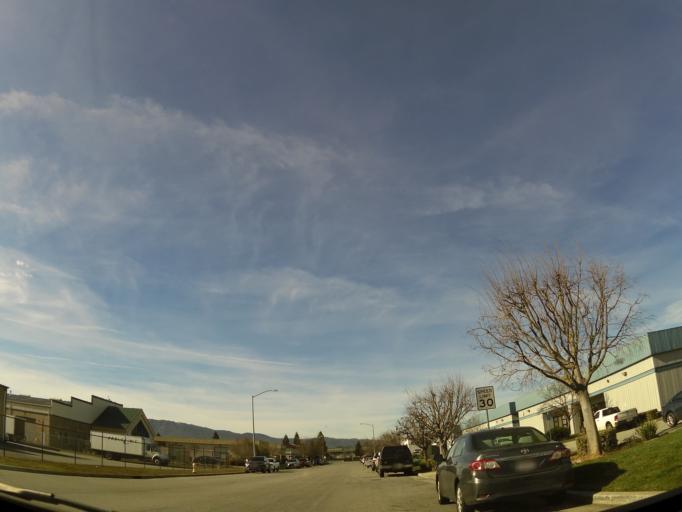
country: US
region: California
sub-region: Santa Clara County
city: Gilroy
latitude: 37.0274
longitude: -121.5726
